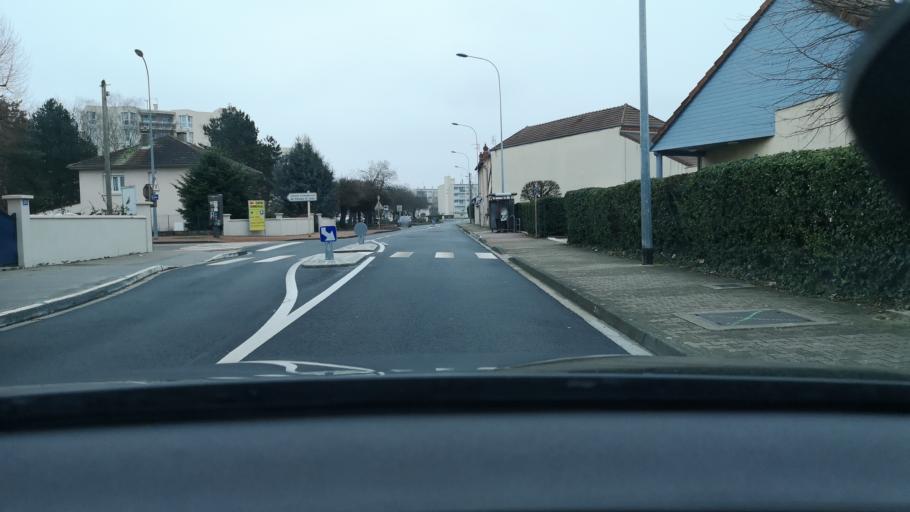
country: FR
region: Bourgogne
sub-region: Departement de Saone-et-Loire
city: Chalon-sur-Saone
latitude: 46.8017
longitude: 4.8547
